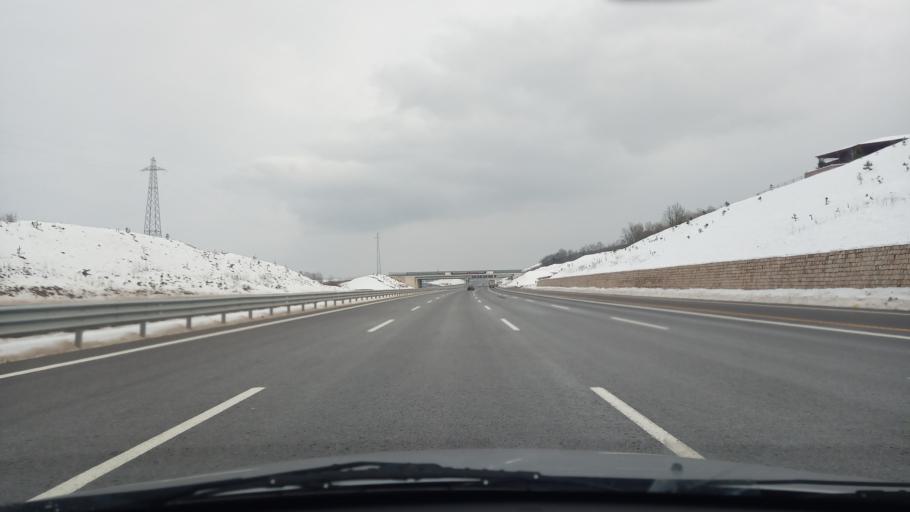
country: TR
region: Kocaeli
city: Derince
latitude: 40.8634
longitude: 29.8414
